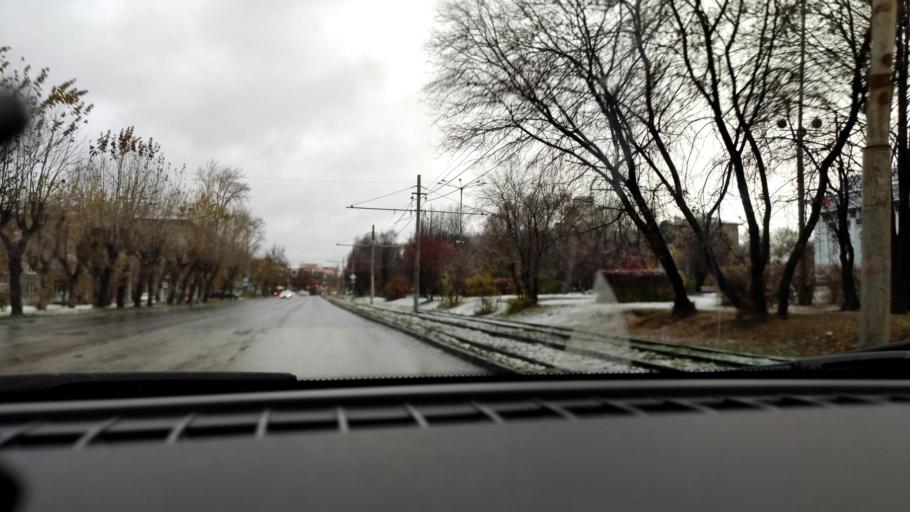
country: RU
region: Perm
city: Perm
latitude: 58.0236
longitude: 56.2874
